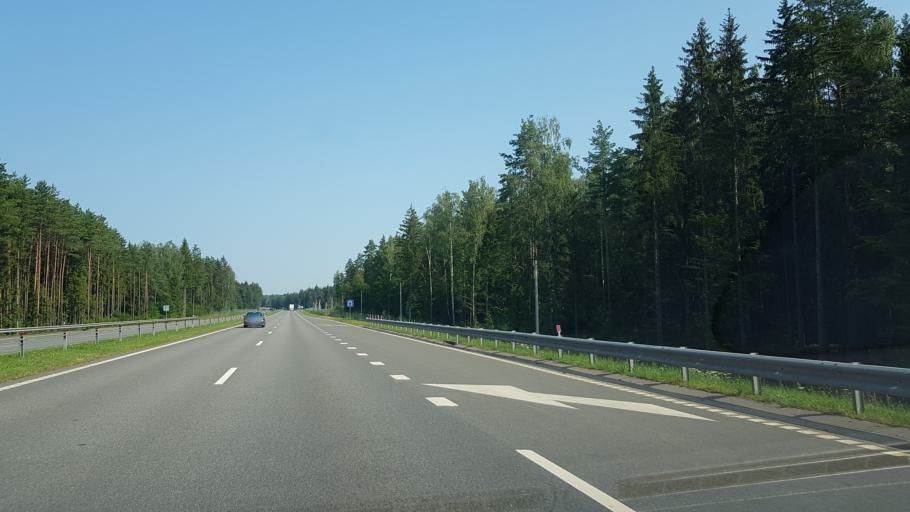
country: BY
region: Mogilev
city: Kirawsk
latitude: 53.2116
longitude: 29.3443
